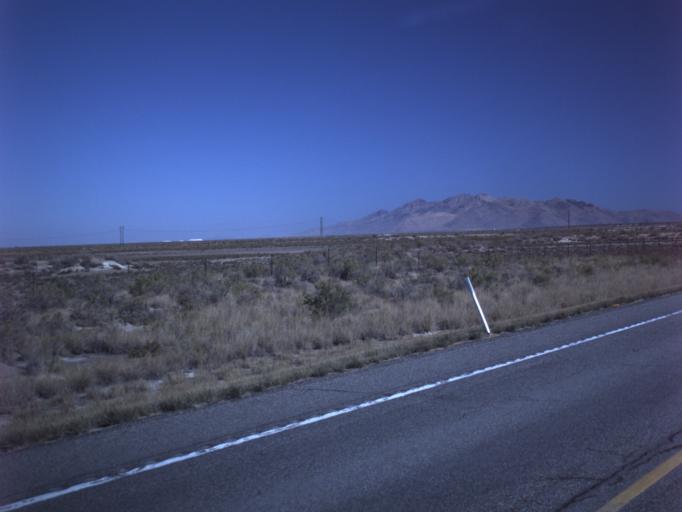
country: US
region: Utah
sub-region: Tooele County
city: Grantsville
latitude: 40.6865
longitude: -112.5417
